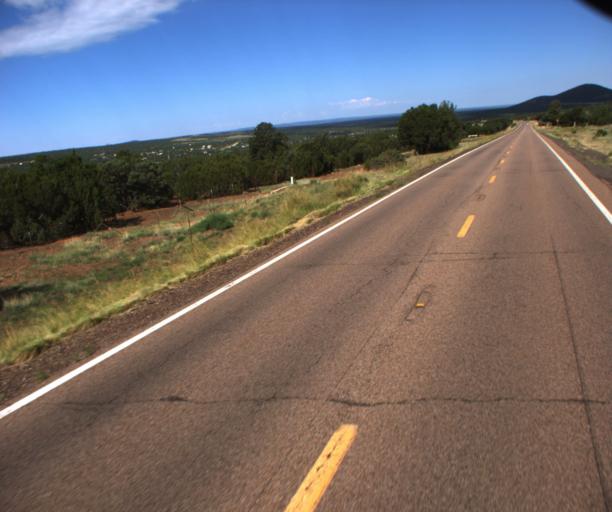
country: US
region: Arizona
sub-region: Navajo County
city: White Mountain Lake
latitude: 34.2827
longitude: -109.8120
